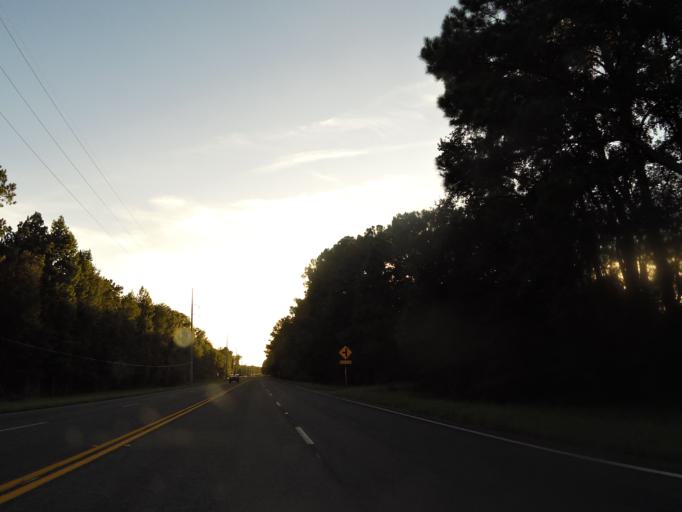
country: US
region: Georgia
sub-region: Camden County
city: Woodbine
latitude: 31.1014
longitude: -81.7027
